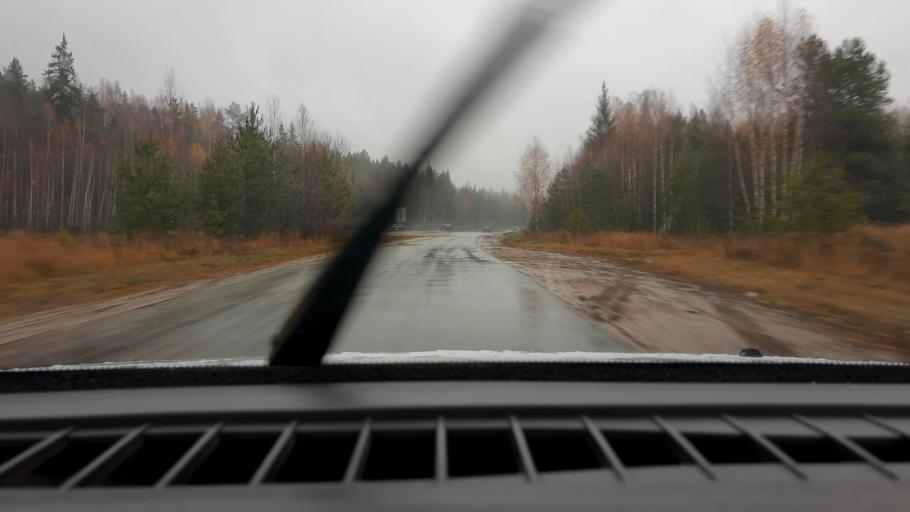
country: RU
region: Nizjnij Novgorod
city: Linda
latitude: 56.6957
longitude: 44.2067
